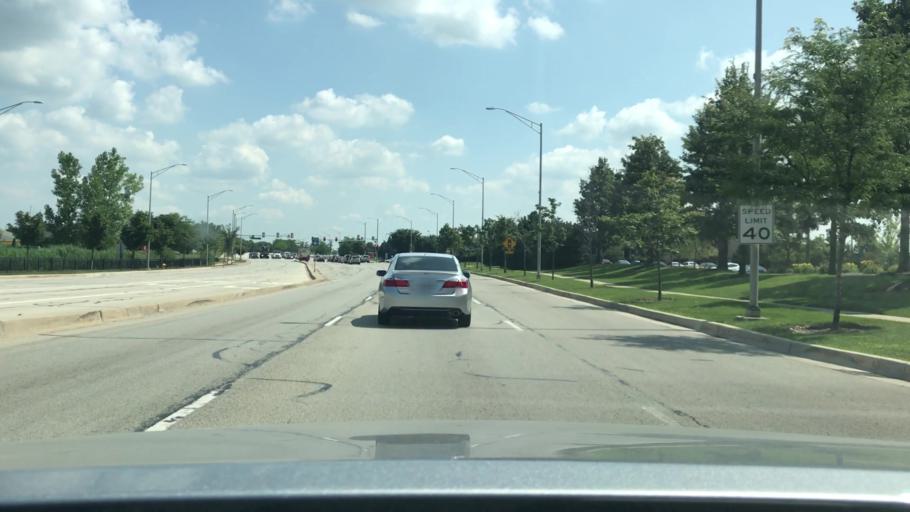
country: US
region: Illinois
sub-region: DuPage County
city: Woodridge
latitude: 41.7213
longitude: -88.0419
